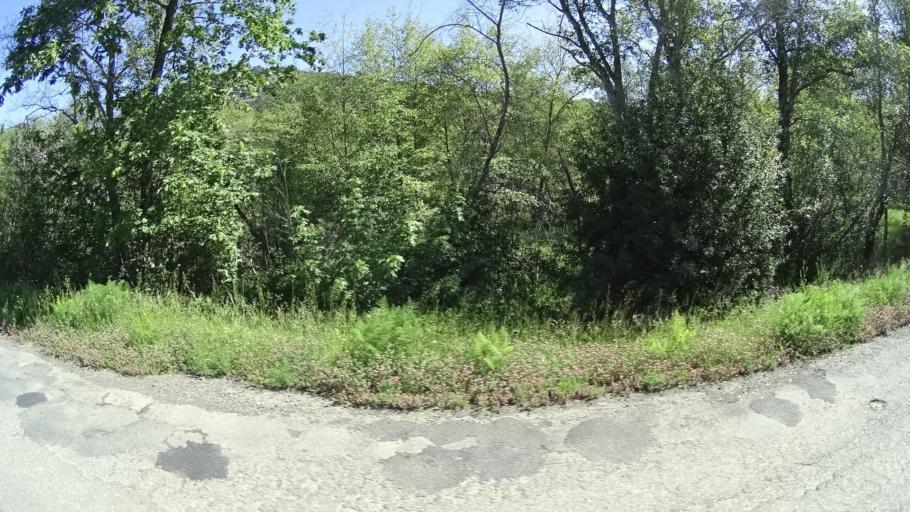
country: US
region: California
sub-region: Humboldt County
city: Rio Dell
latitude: 40.2362
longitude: -124.1189
